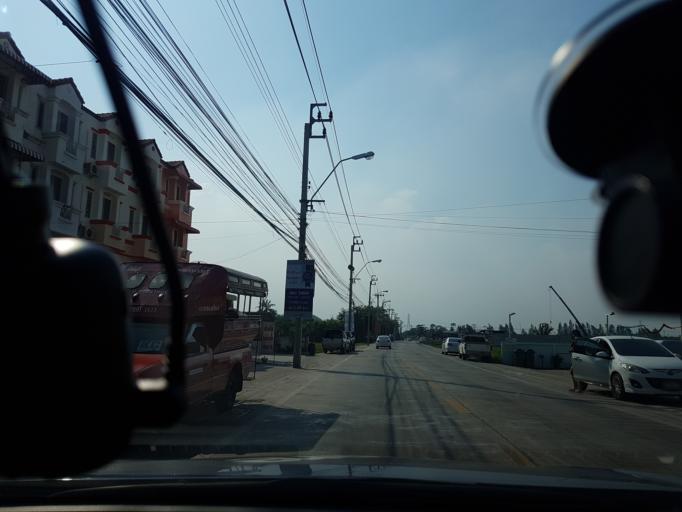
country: TH
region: Pathum Thani
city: Lam Luk Ka
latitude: 13.8962
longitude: 100.7187
